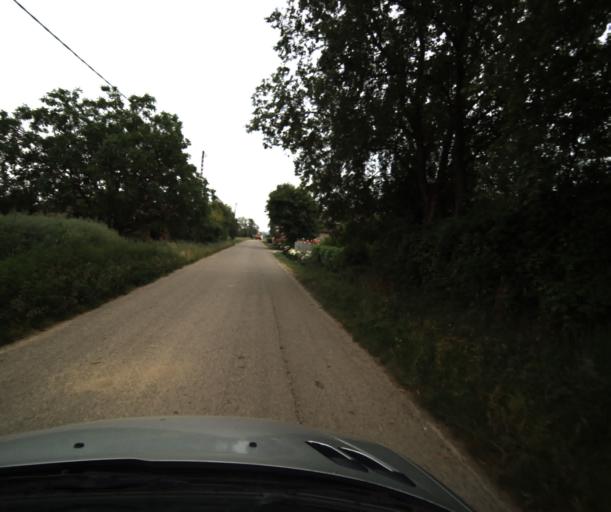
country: FR
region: Midi-Pyrenees
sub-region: Departement du Tarn-et-Garonne
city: Saint-Nicolas-de-la-Grave
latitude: 44.0575
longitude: 0.9745
